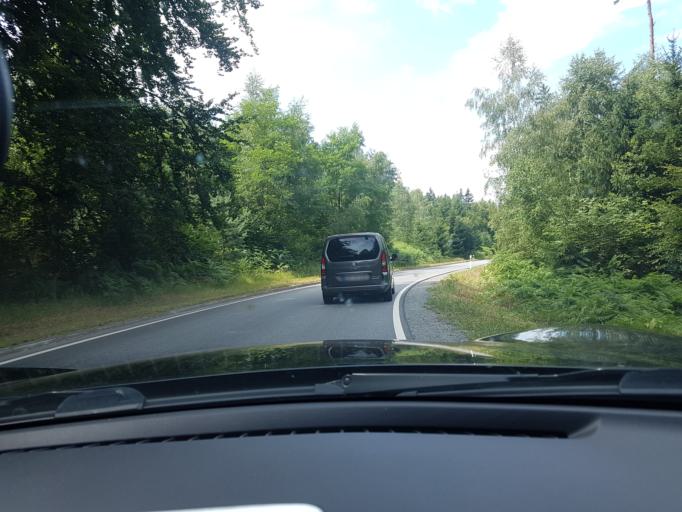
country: DE
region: Hesse
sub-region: Regierungsbezirk Darmstadt
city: Rothenberg
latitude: 49.5356
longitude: 8.9395
